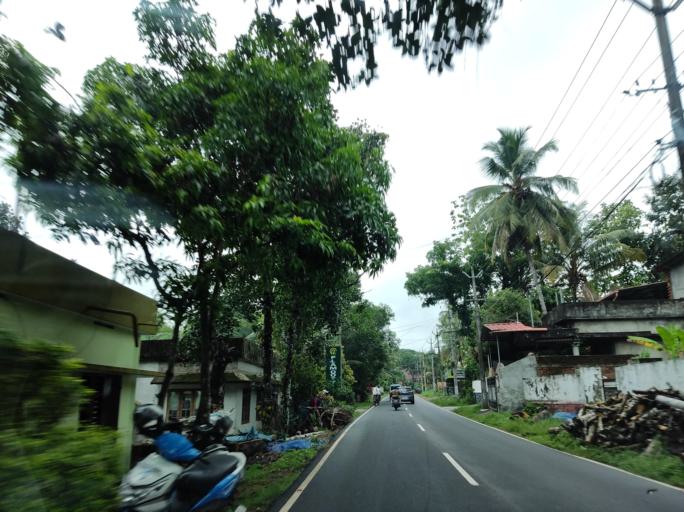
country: IN
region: Kerala
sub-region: Alappuzha
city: Mavelikara
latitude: 9.2364
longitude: 76.5578
